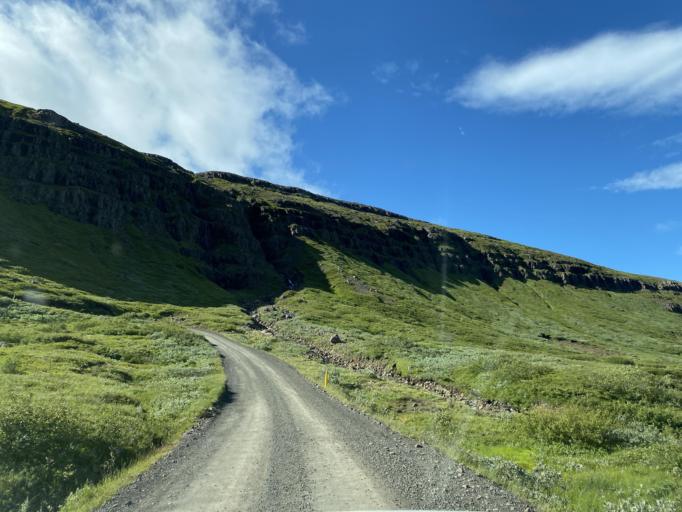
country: IS
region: East
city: Eskifjoerdur
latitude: 65.1826
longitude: -14.0804
